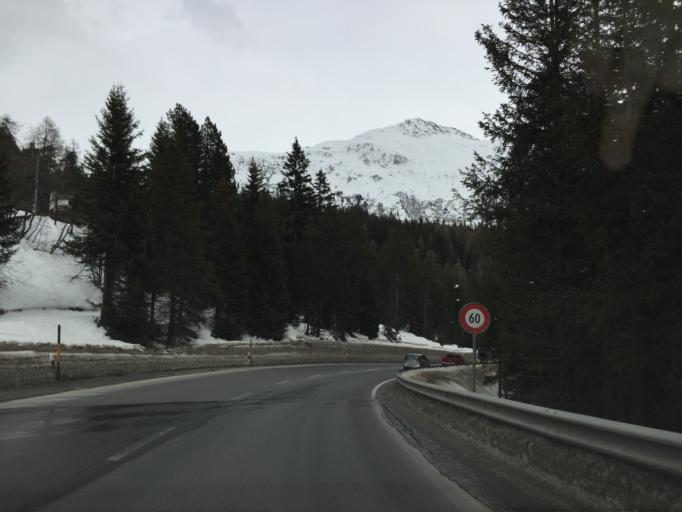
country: CH
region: Grisons
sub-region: Praettigau/Davos District
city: Davos
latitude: 46.8315
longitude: 9.8548
